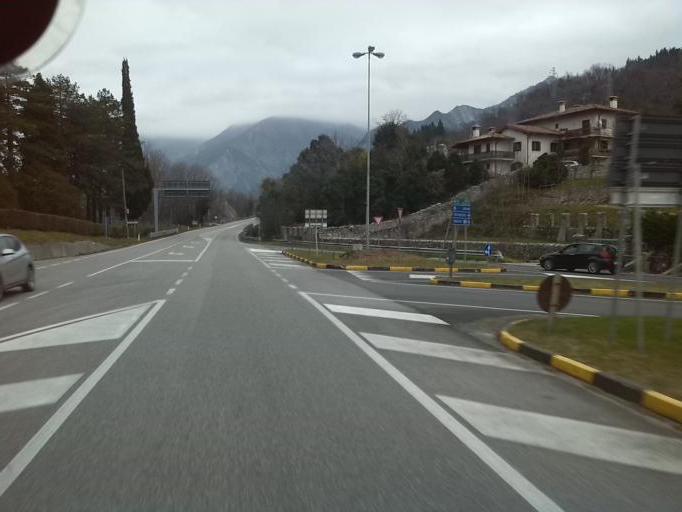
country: IT
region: Friuli Venezia Giulia
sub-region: Provincia di Udine
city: Bordano
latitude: 46.3018
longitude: 13.1196
